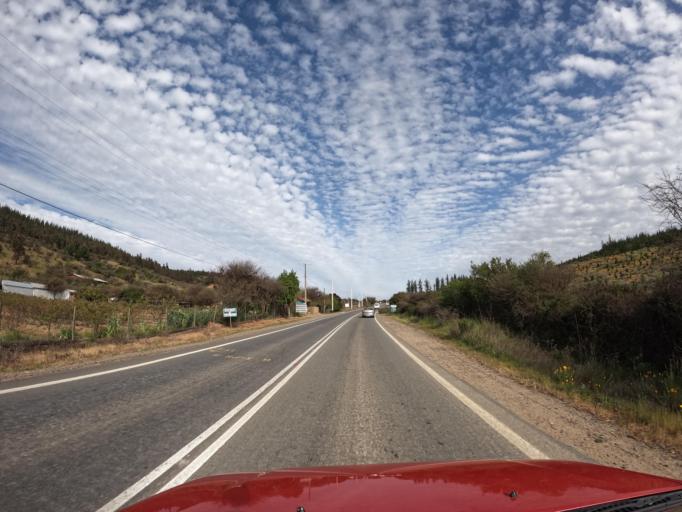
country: CL
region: O'Higgins
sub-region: Provincia de Colchagua
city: Santa Cruz
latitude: -34.3094
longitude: -71.7776
